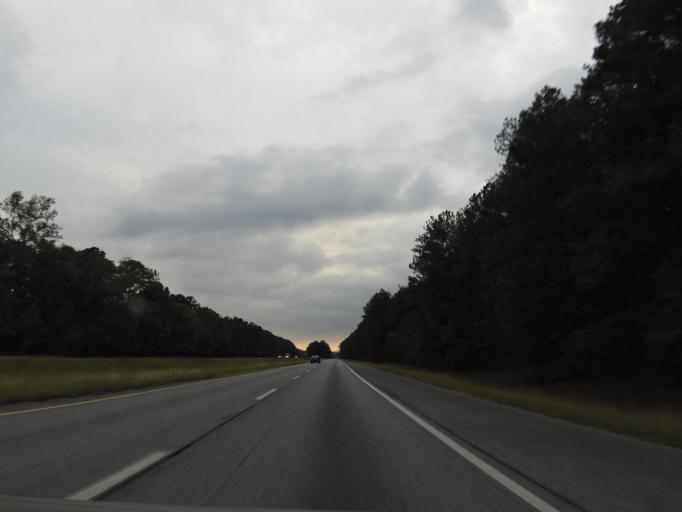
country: US
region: Alabama
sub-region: Saint Clair County
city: Ashville
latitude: 33.8090
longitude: -86.3600
